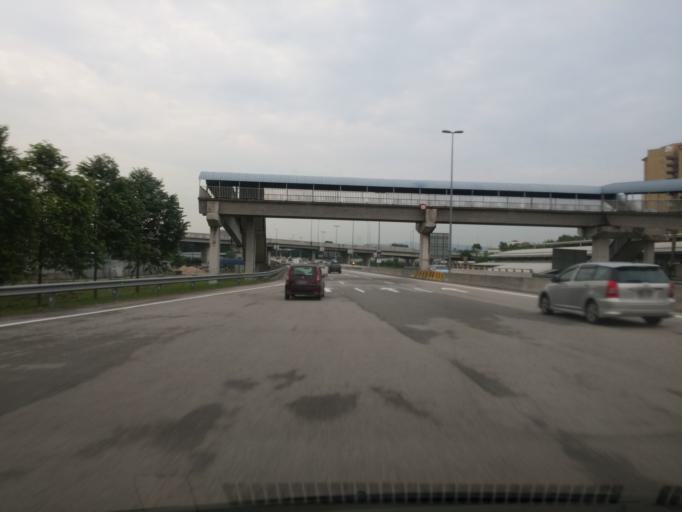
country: MY
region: Kuala Lumpur
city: Kuala Lumpur
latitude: 3.1125
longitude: 101.7136
